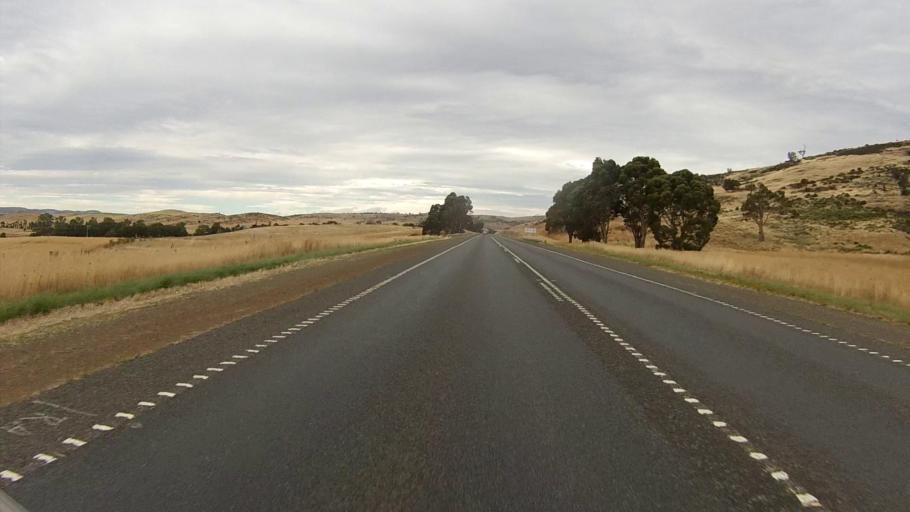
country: AU
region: Tasmania
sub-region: Brighton
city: Bridgewater
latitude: -42.3801
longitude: 147.3209
